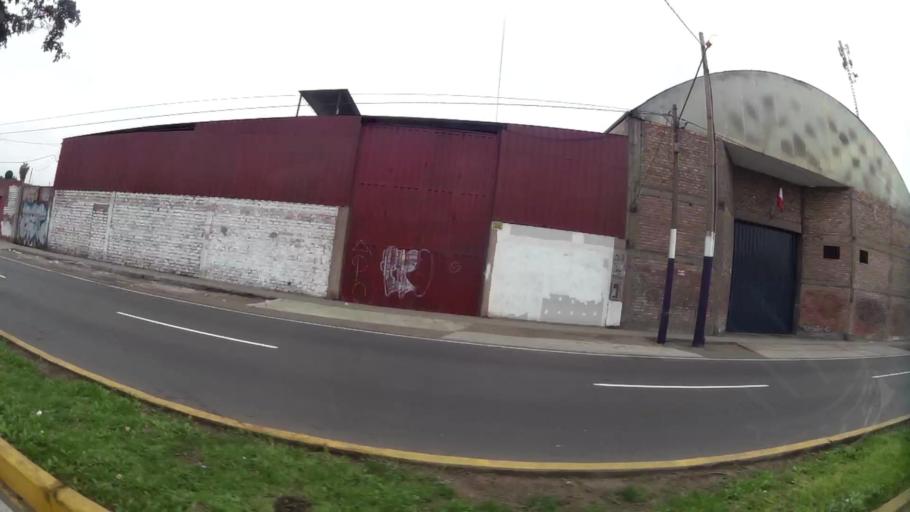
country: PE
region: Lima
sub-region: Lima
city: Surco
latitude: -12.1938
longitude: -77.0087
